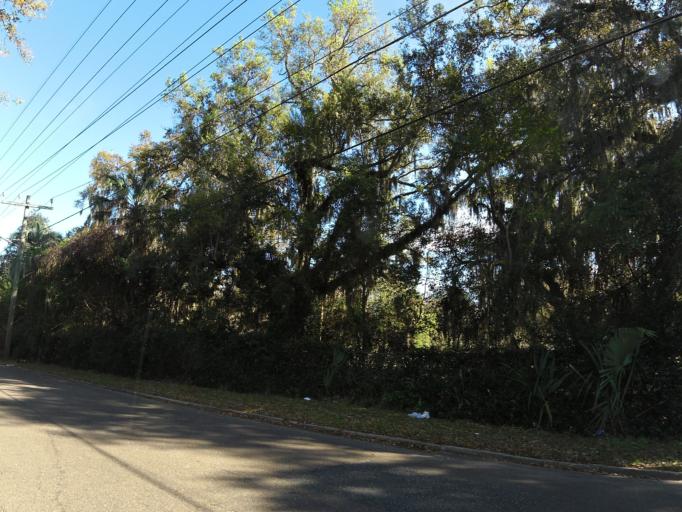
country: US
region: Florida
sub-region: Duval County
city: Jacksonville
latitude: 30.3727
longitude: -81.6445
